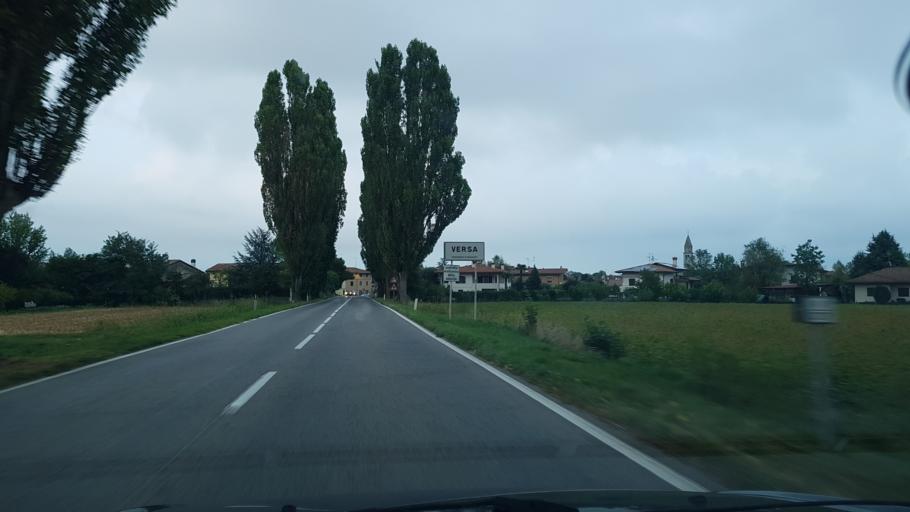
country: IT
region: Friuli Venezia Giulia
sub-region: Provincia di Gorizia
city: Medea
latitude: 45.8984
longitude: 13.4138
